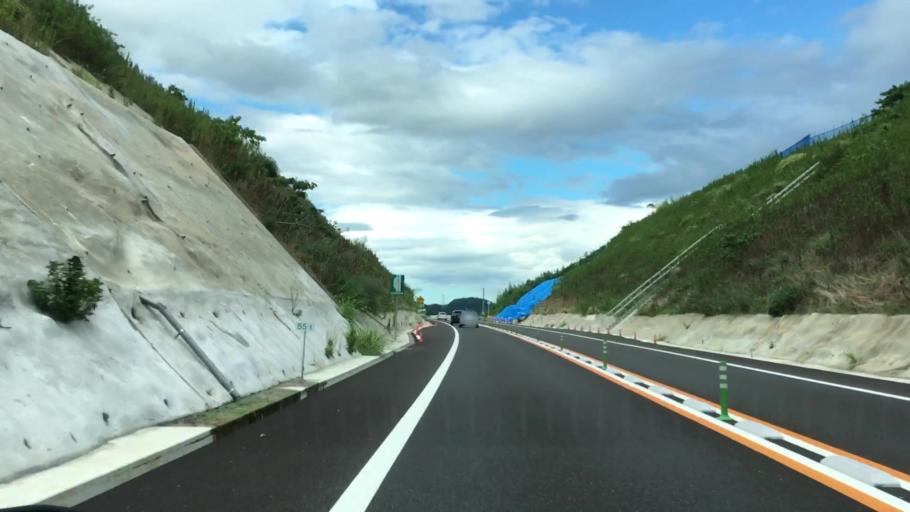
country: JP
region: Saga Prefecture
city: Imaricho-ko
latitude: 33.3216
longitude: 129.9261
